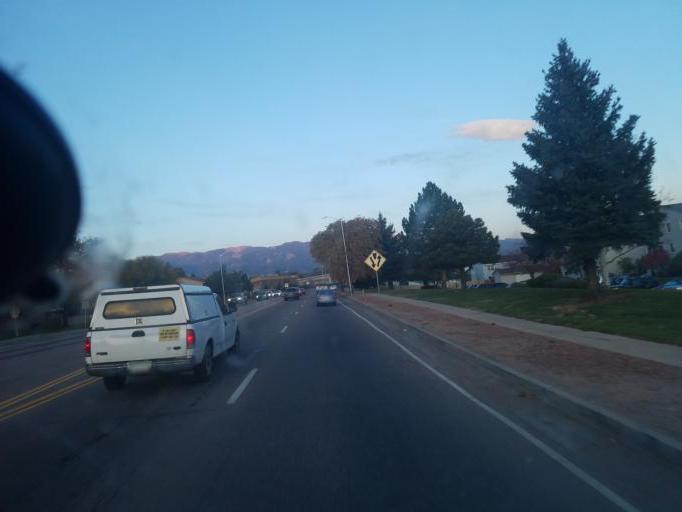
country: US
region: Colorado
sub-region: El Paso County
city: Stratmoor
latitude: 38.8152
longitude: -104.7670
